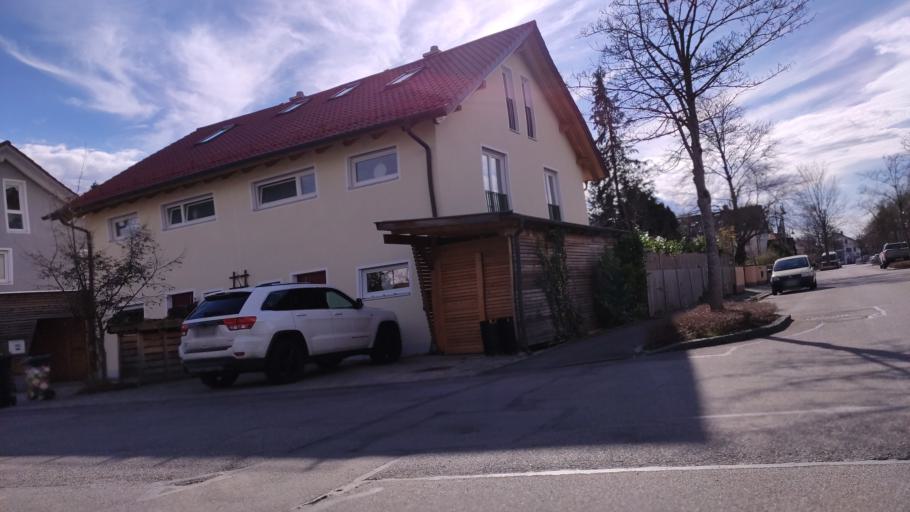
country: DE
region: Bavaria
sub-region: Upper Bavaria
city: Emmering
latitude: 48.1895
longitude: 11.2765
